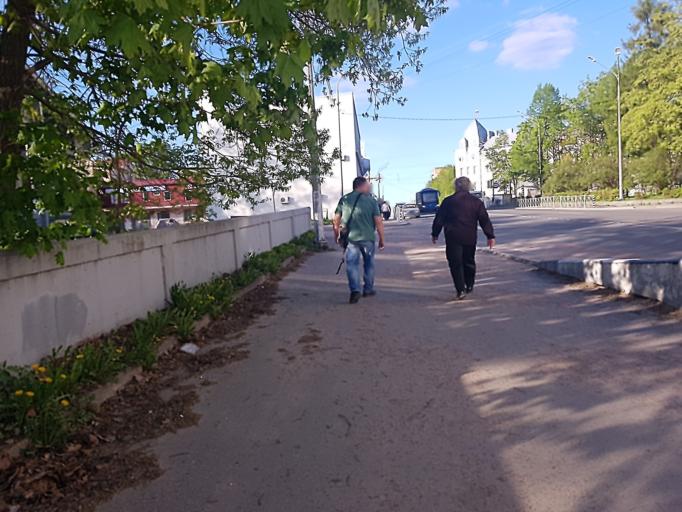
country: RU
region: Republic of Karelia
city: Sortavala
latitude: 61.7016
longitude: 30.6878
